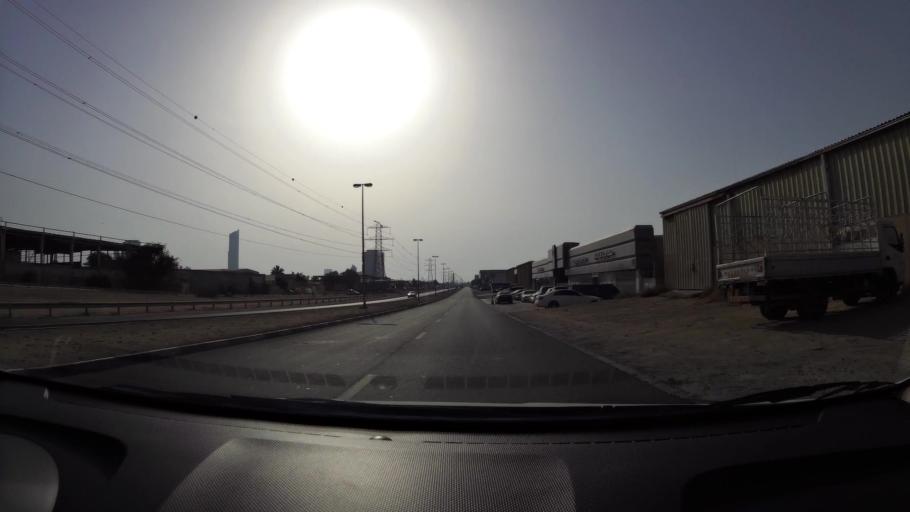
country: AE
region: Ash Shariqah
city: Sharjah
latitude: 25.2276
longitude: 55.3650
